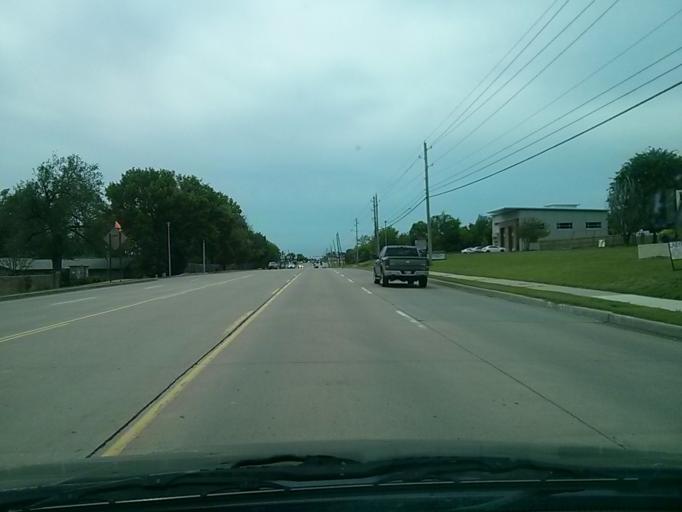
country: US
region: Oklahoma
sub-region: Tulsa County
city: Jenks
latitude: 36.0666
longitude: -95.9044
